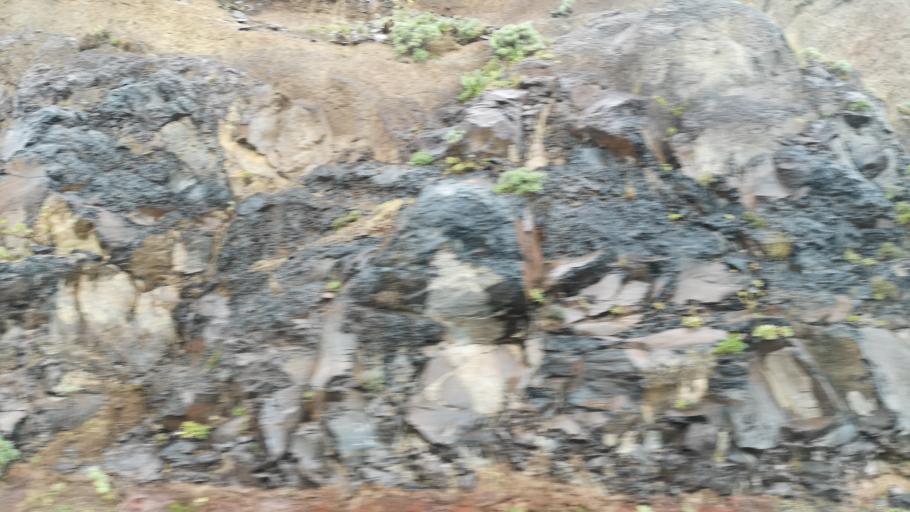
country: ES
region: Canary Islands
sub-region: Provincia de Santa Cruz de Tenerife
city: Alajero
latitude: 28.0932
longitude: -17.1967
